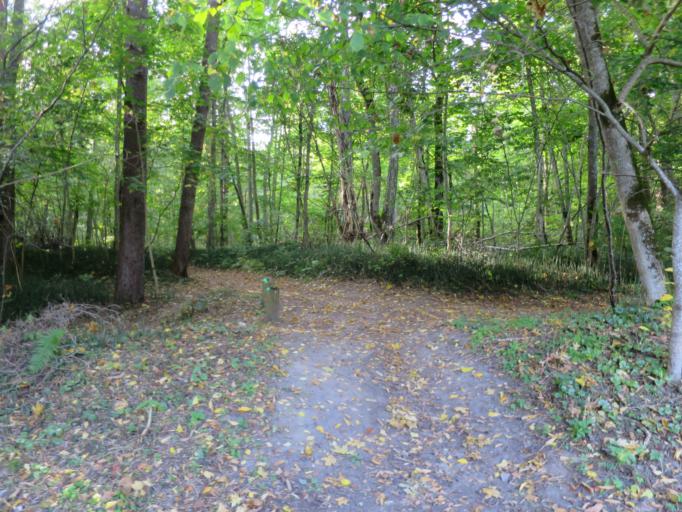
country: LV
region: Sigulda
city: Sigulda
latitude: 57.1666
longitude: 24.8383
